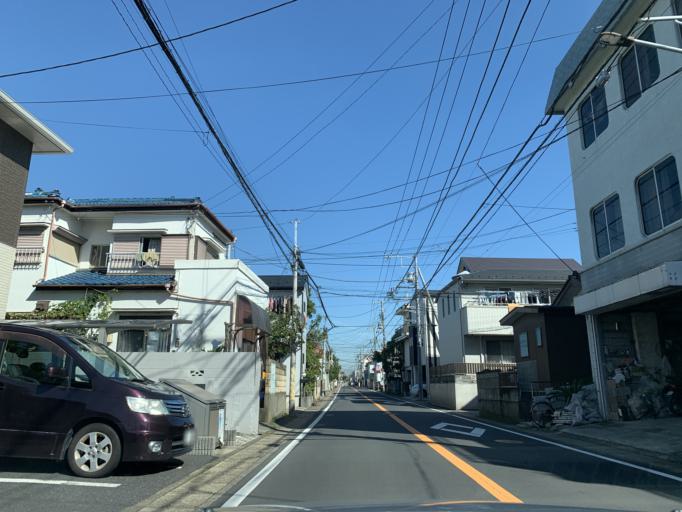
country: JP
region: Tokyo
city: Urayasu
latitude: 35.6820
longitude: 139.9037
